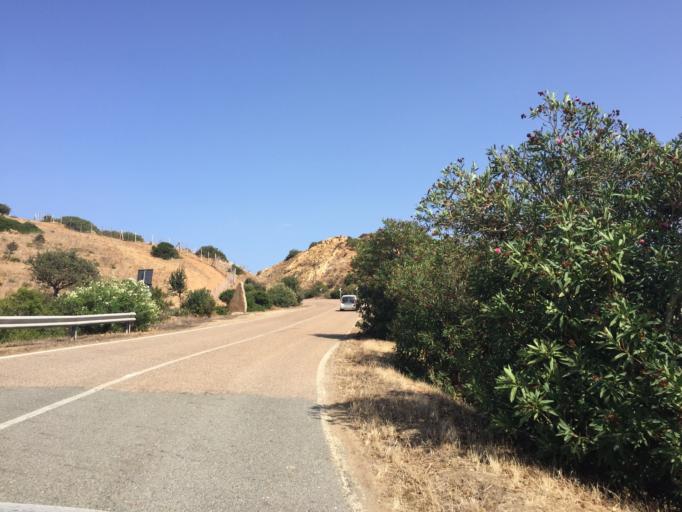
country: IT
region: Sardinia
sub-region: Provincia di Cagliari
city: Villasimius
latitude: 39.1565
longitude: 9.5590
